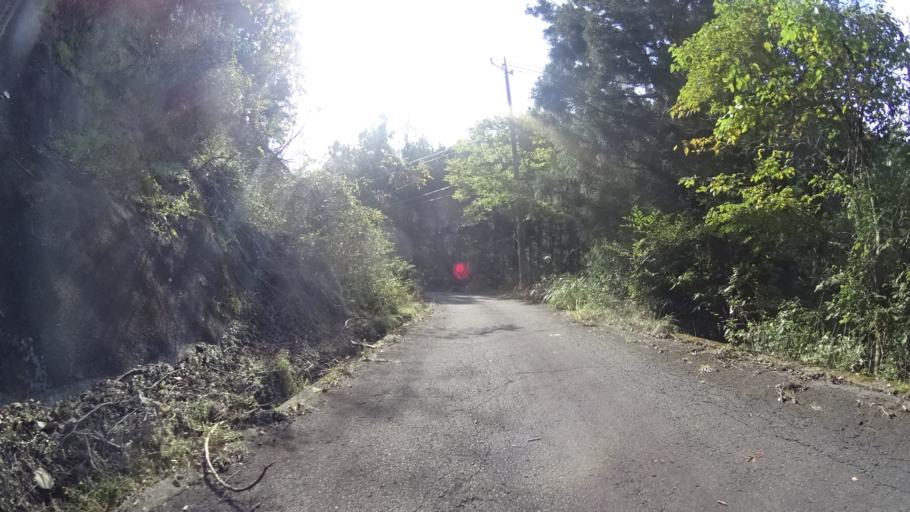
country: JP
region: Yamanashi
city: Otsuki
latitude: 35.5780
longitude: 138.9816
